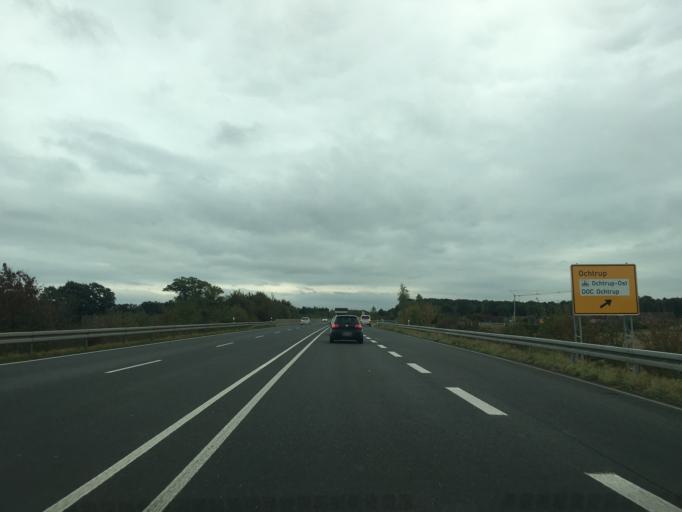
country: DE
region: North Rhine-Westphalia
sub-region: Regierungsbezirk Munster
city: Ochtrup
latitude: 52.1909
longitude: 7.2155
